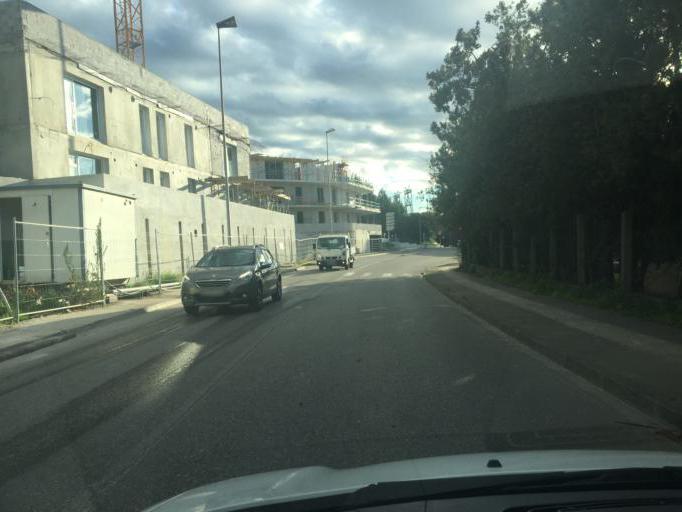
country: FR
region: Provence-Alpes-Cote d'Azur
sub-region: Departement des Bouches-du-Rhone
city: Martigues
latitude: 43.4098
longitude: 5.0456
